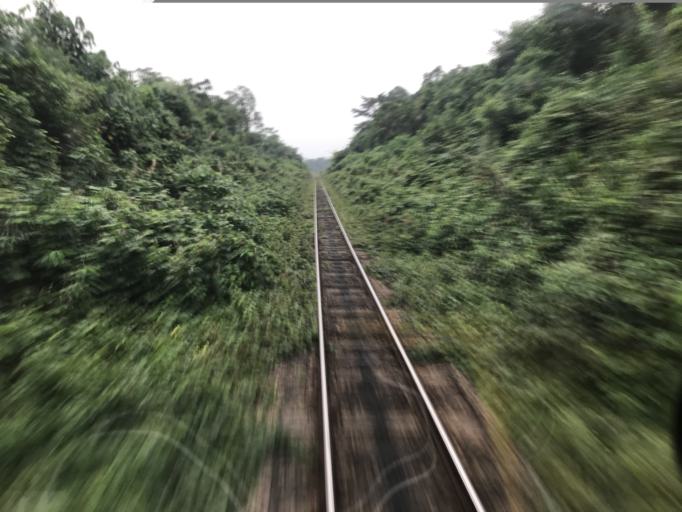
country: CM
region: Littoral
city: Edea
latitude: 3.9477
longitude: 10.0887
